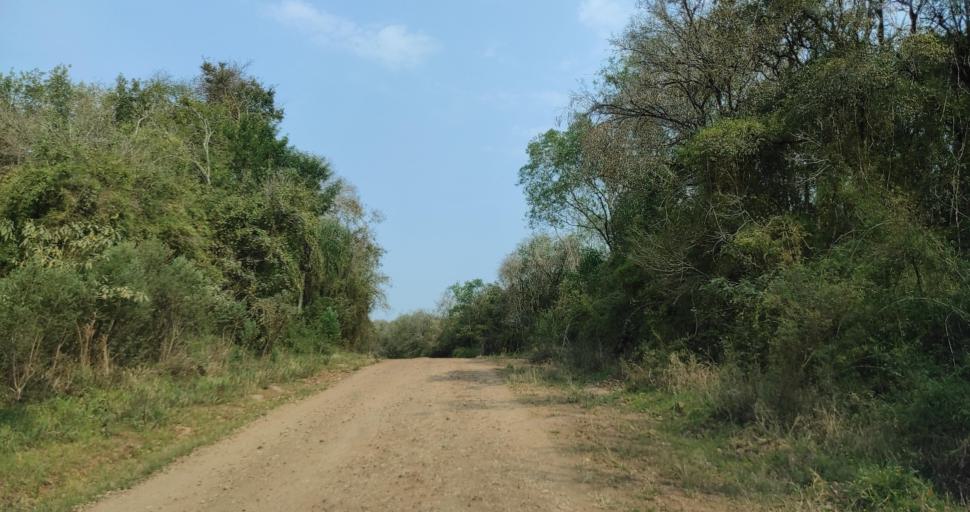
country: AR
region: Misiones
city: Cerro Cora
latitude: -27.5436
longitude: -55.5845
